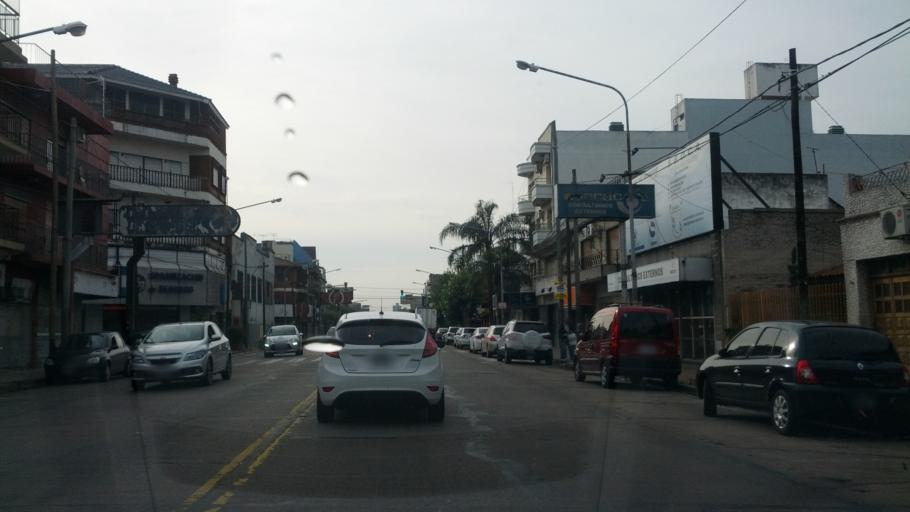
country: AR
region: Buenos Aires
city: San Justo
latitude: -34.6607
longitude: -58.5430
